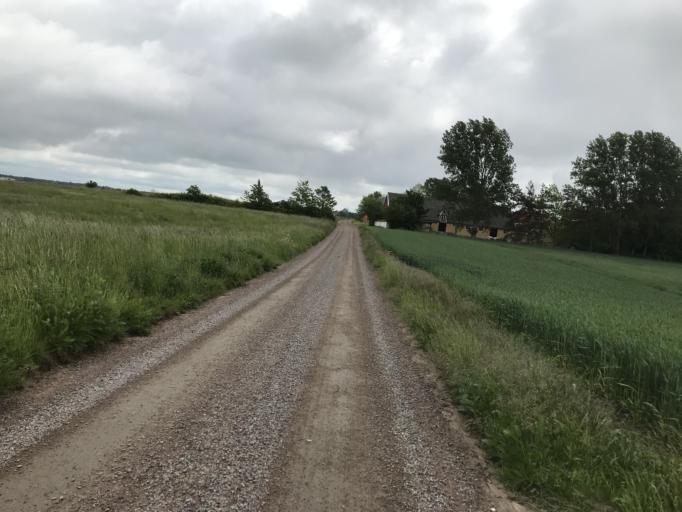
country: SE
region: Skane
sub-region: Landskrona
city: Asmundtorp
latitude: 55.8694
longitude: 12.9132
